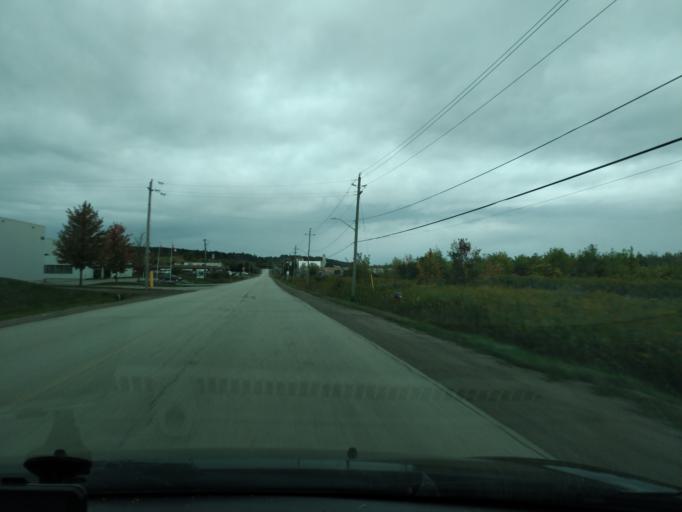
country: CA
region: Ontario
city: Bradford West Gwillimbury
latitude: 44.1330
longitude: -79.5554
